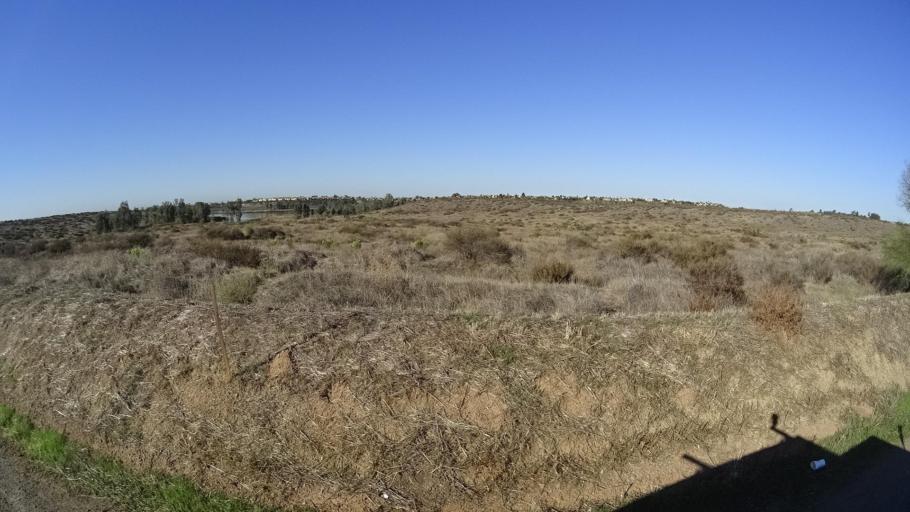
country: US
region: California
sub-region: San Diego County
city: Jamul
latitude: 32.6394
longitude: -116.9226
